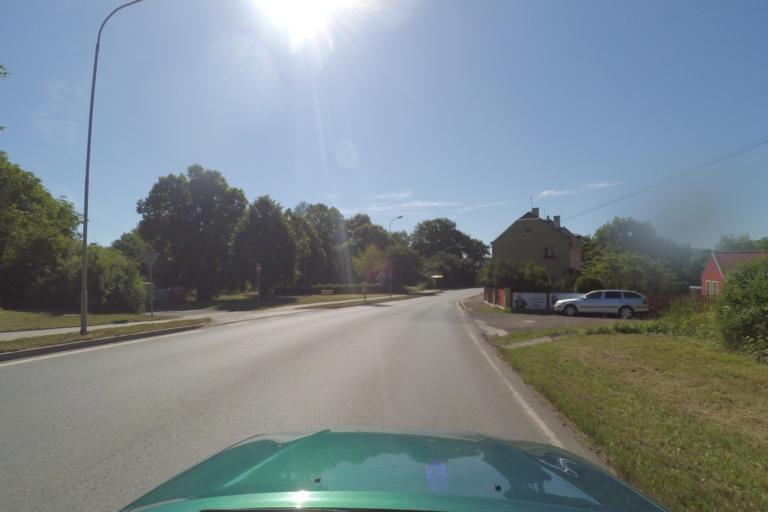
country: CZ
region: Karlovarsky
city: Nova Role
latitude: 50.2374
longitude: 12.8075
